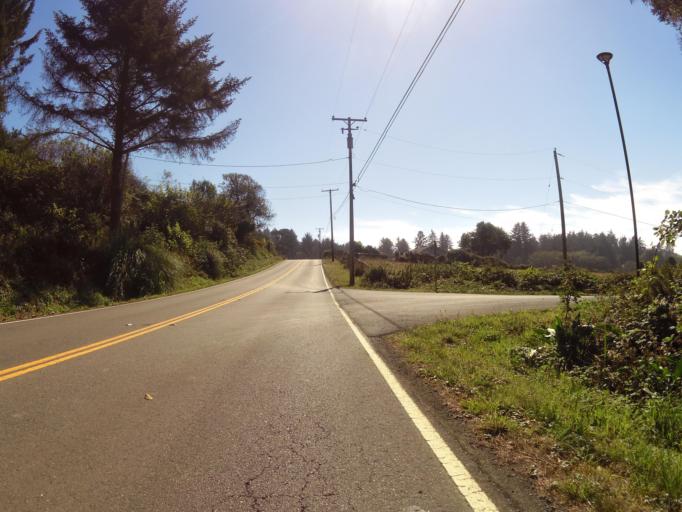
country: US
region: Oregon
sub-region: Curry County
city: Harbor
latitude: 41.9627
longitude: -124.1988
